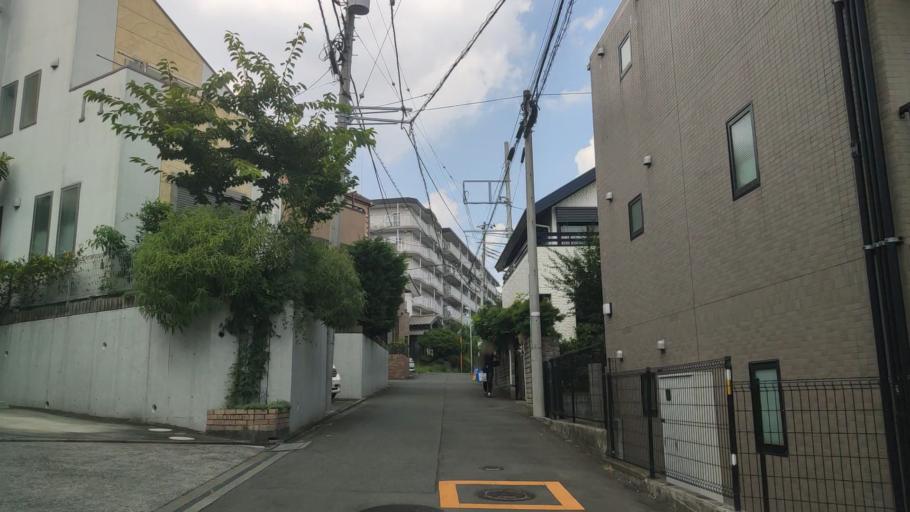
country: JP
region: Tokyo
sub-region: Machida-shi
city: Machida
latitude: 35.5395
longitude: 139.4405
